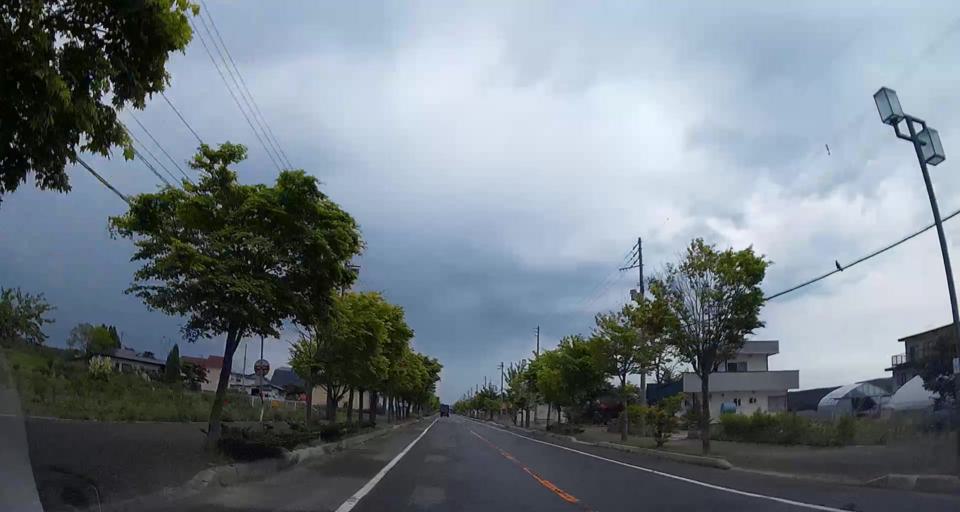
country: JP
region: Hokkaido
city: Chitose
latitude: 42.7285
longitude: 141.8827
